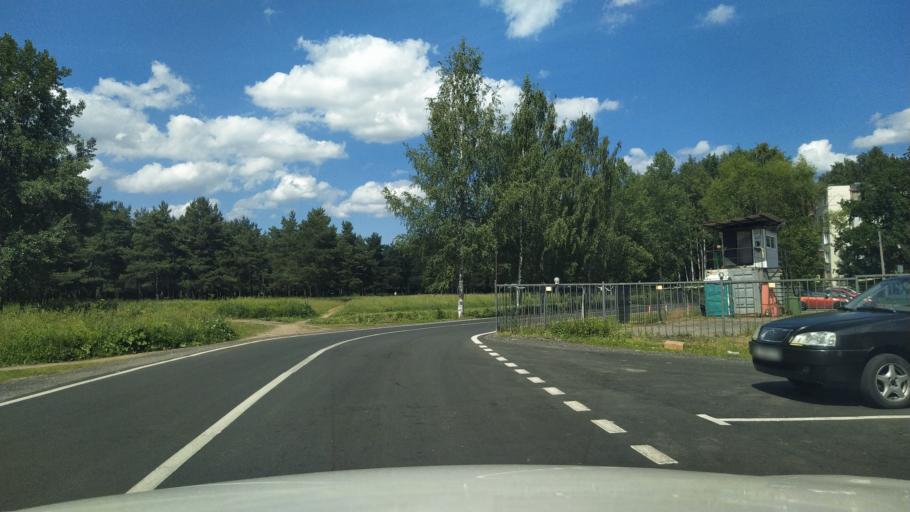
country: RU
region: Leningrad
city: Akademicheskoe
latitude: 60.0012
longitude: 30.4207
